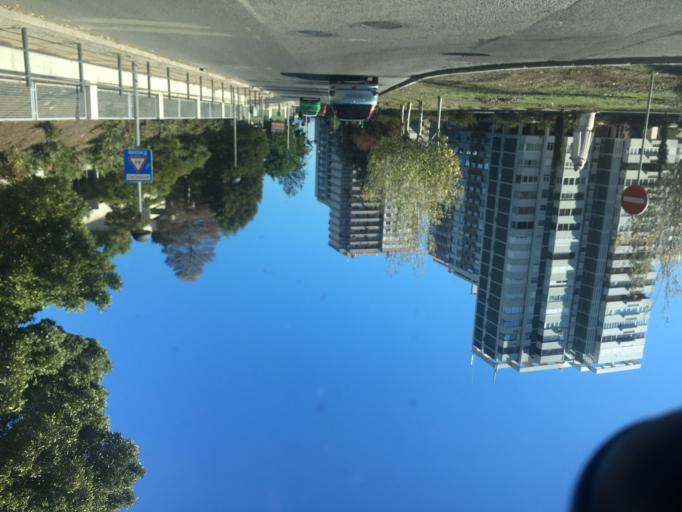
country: PT
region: Lisbon
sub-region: Oeiras
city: Alges
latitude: 38.7116
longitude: -9.2102
